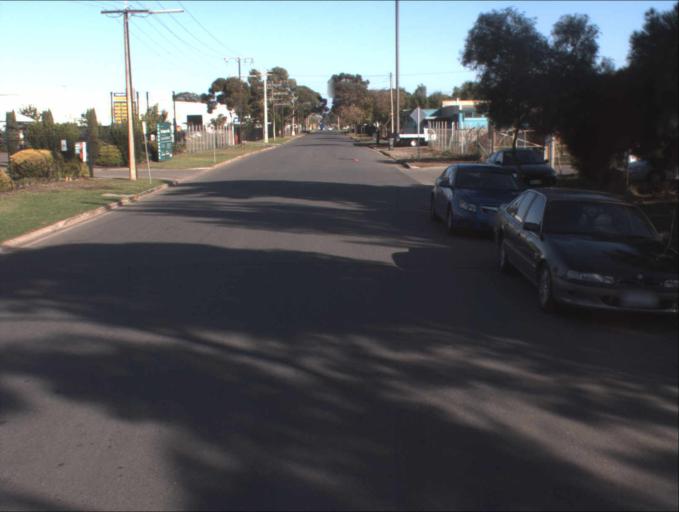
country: AU
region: South Australia
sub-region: Charles Sturt
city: Woodville North
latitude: -34.8454
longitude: 138.5583
